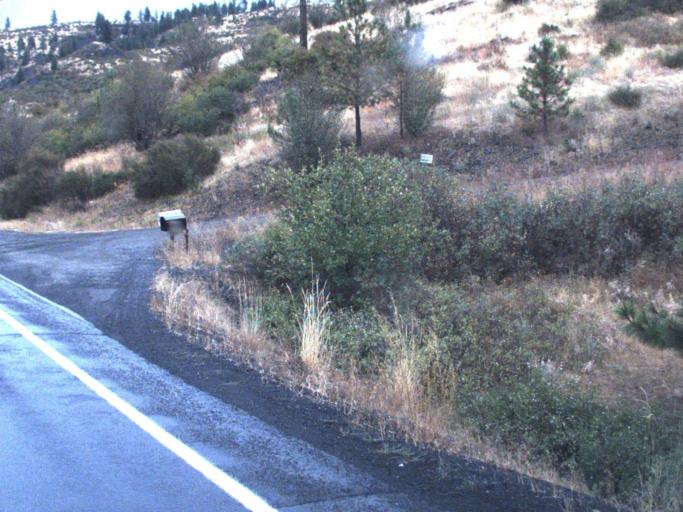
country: US
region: Washington
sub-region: Lincoln County
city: Davenport
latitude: 47.7758
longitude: -117.8915
